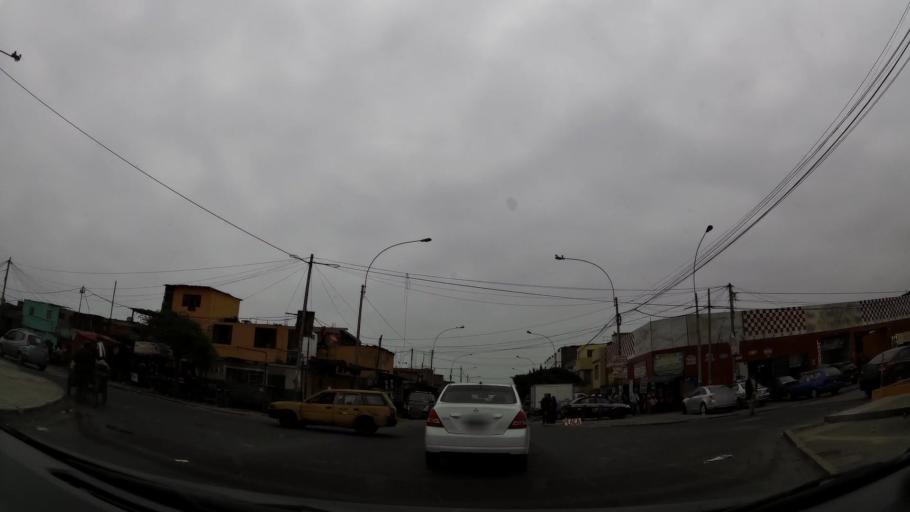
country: PE
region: Lima
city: Lima
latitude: -12.0533
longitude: -77.0638
